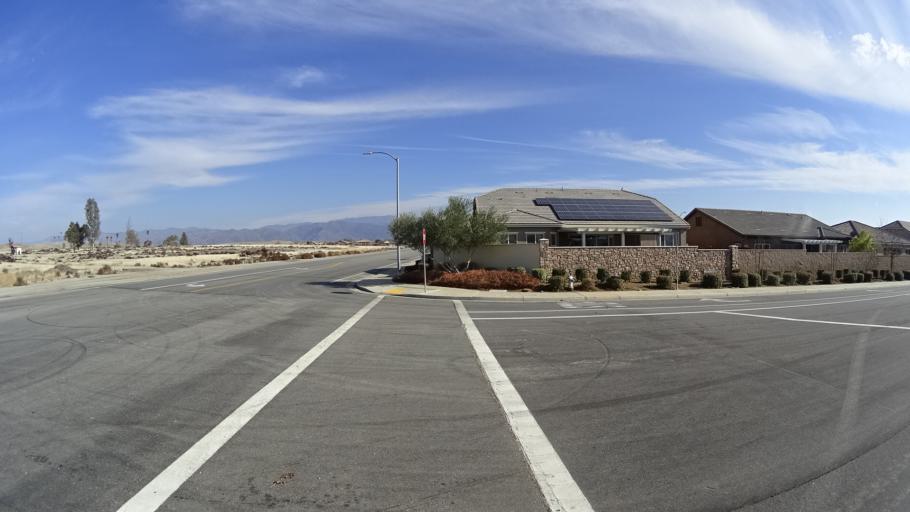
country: US
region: California
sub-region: Kern County
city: Oildale
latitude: 35.4124
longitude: -118.8965
